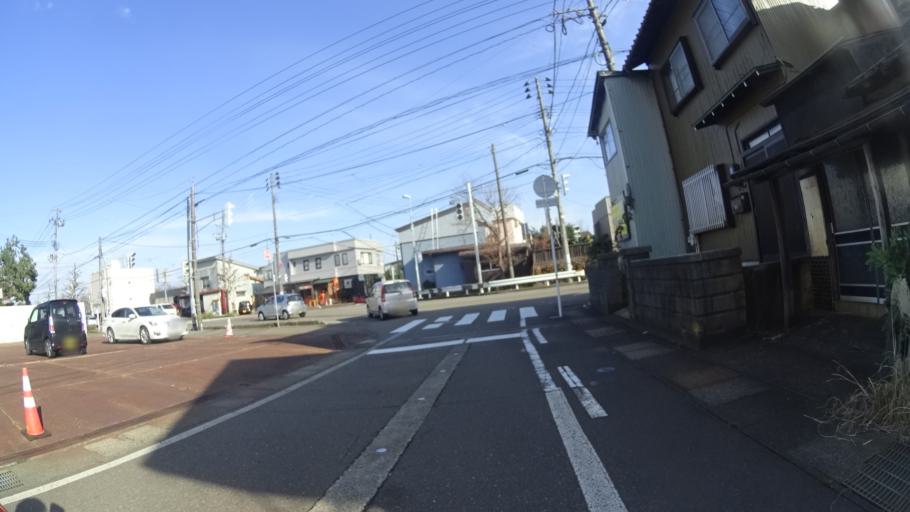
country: JP
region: Niigata
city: Joetsu
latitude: 37.1056
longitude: 138.2487
